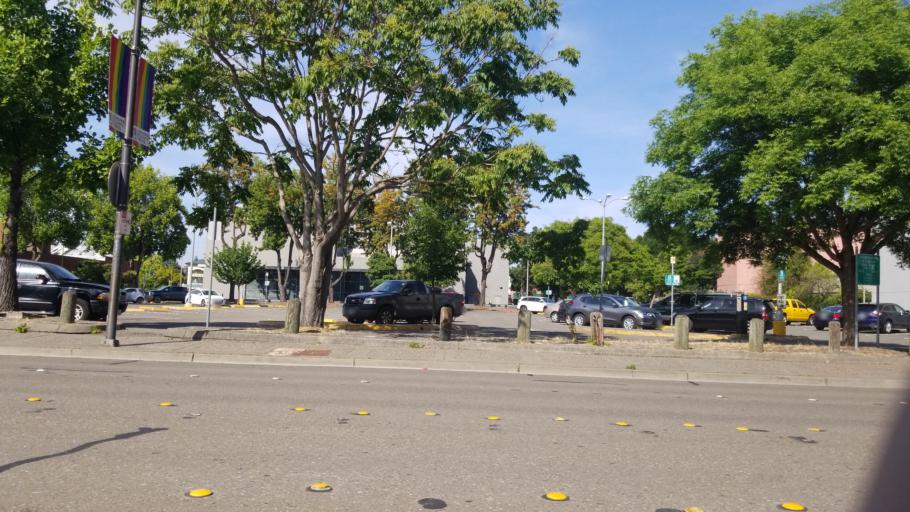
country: US
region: California
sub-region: Sonoma County
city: Santa Rosa
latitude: 38.4411
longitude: -122.7167
